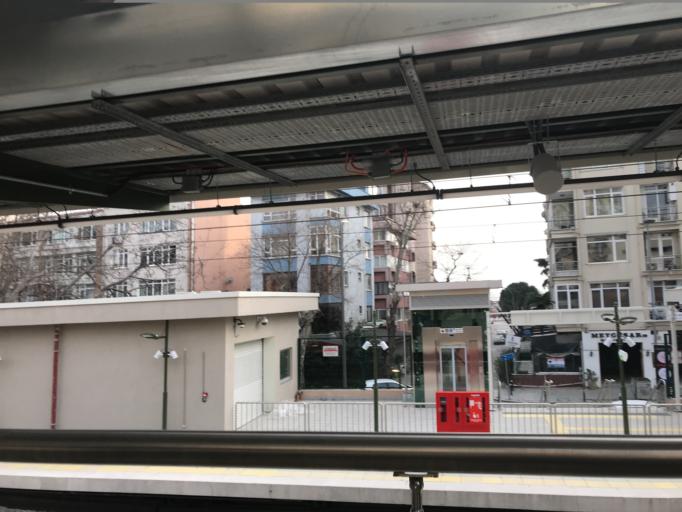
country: TR
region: Istanbul
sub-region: Atasehir
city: Atasehir
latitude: 40.9542
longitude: 29.0942
